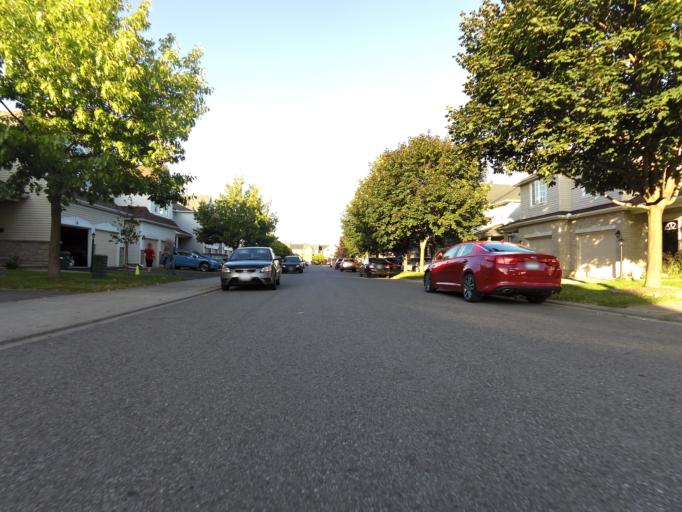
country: CA
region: Ontario
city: Bells Corners
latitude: 45.2788
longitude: -75.7325
